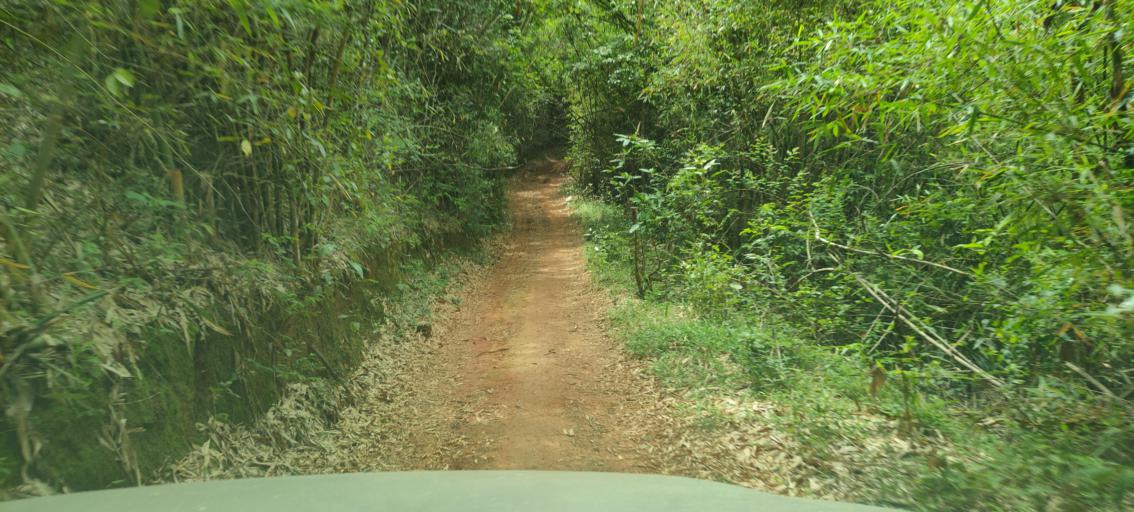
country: LA
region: Loungnamtha
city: Muang Nale
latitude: 20.4157
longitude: 101.4728
